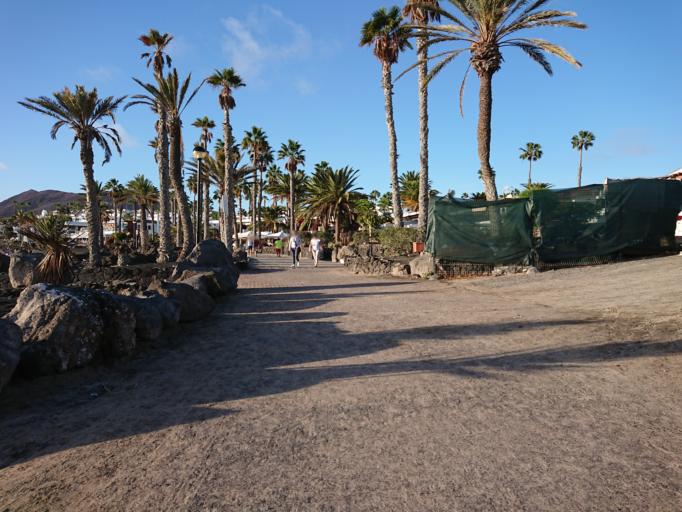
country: ES
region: Canary Islands
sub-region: Provincia de Las Palmas
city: Playa Blanca
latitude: 28.8572
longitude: -13.8408
